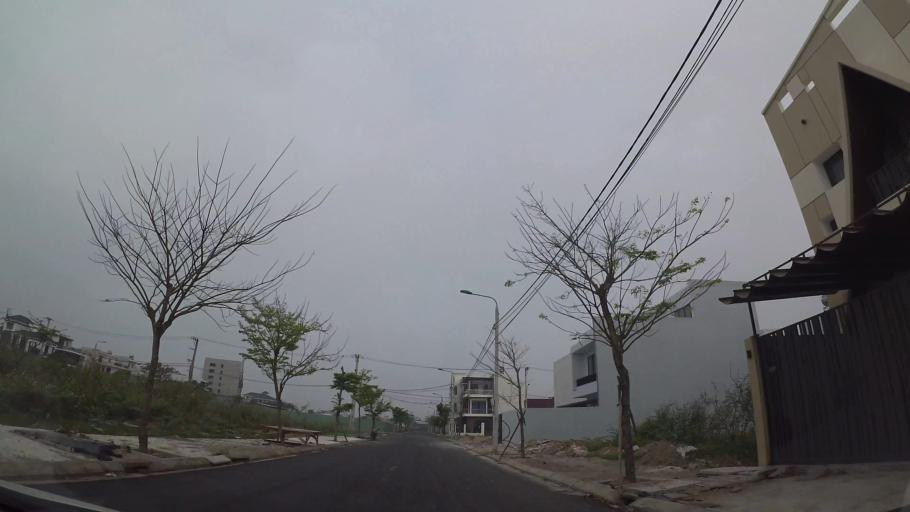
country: VN
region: Da Nang
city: Ngu Hanh Son
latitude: 16.0191
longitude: 108.2339
